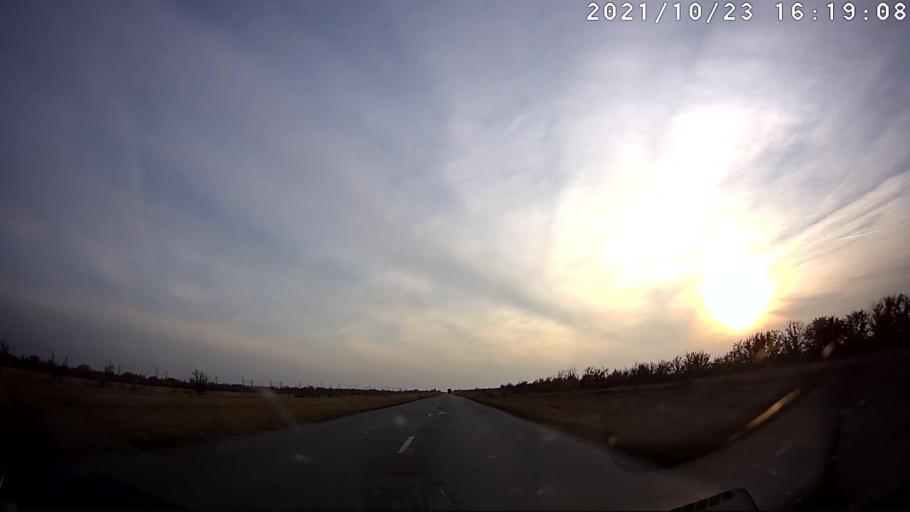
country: RU
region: Volgograd
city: Kotel'nikovo
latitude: 47.8907
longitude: 43.5410
